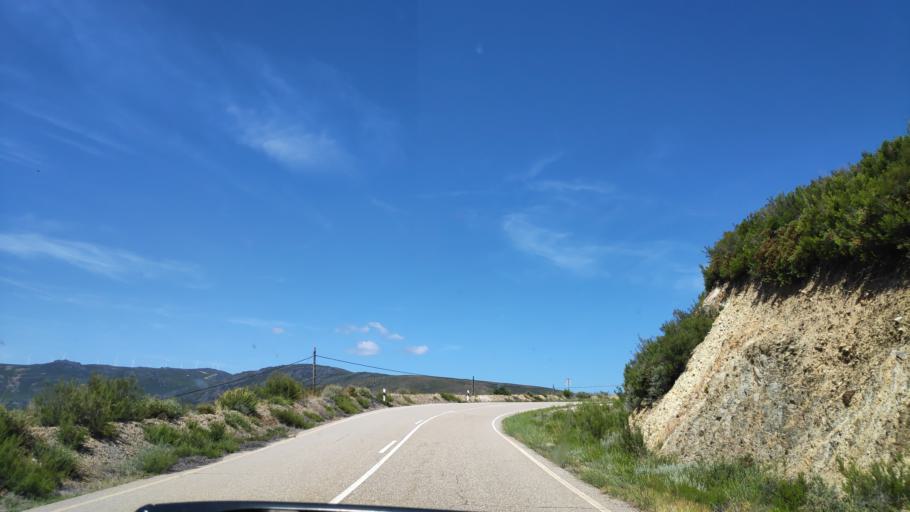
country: ES
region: Castille and Leon
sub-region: Provincia de Zamora
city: Requejo
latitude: 41.9964
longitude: -6.6964
